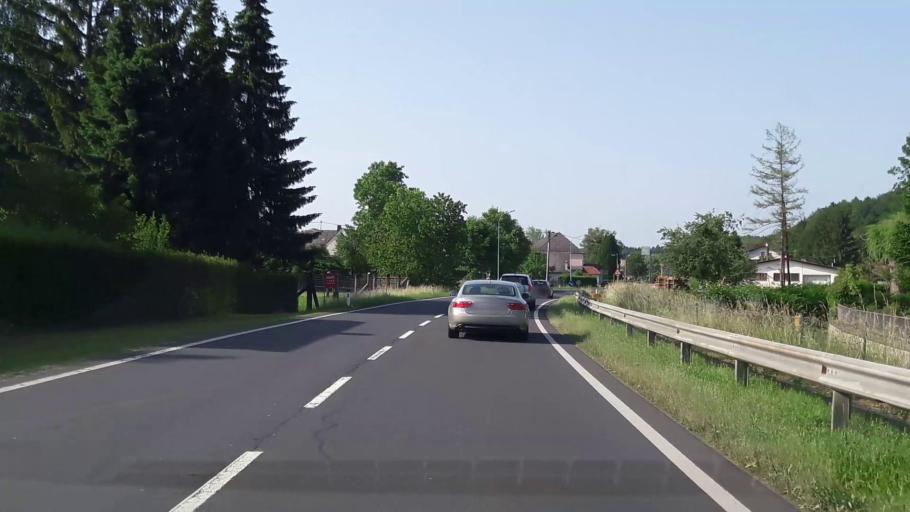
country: AT
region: Burgenland
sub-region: Politischer Bezirk Oberwart
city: Kemeten
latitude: 47.2473
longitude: 16.1518
